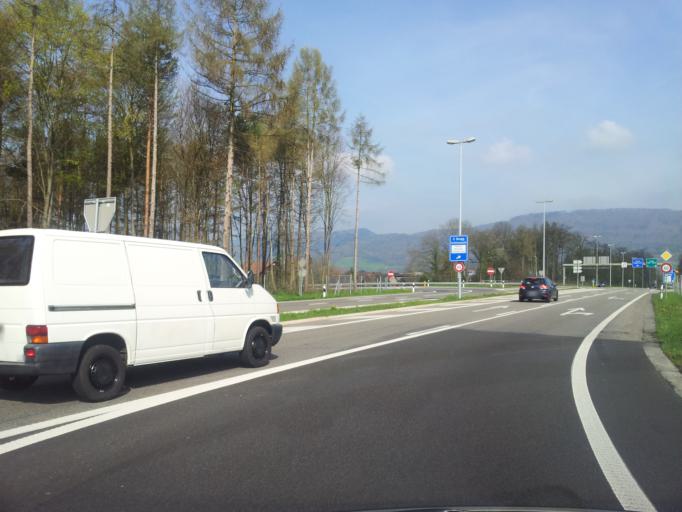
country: CH
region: Aargau
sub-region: Bezirk Brugg
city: Rupperswil
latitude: 47.3927
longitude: 8.1315
